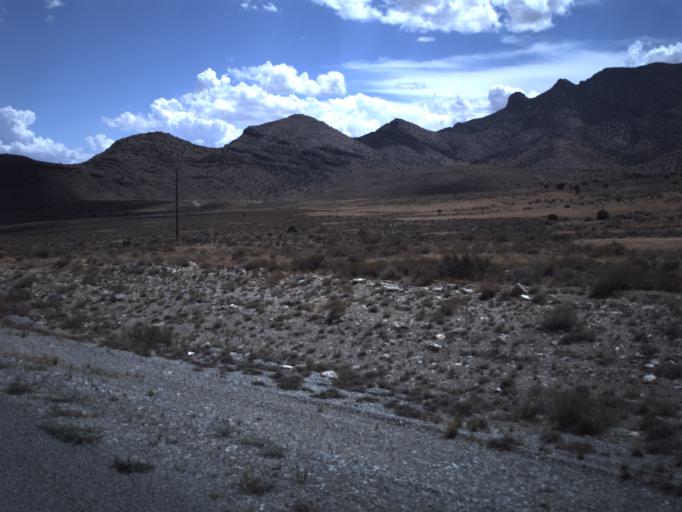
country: US
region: Utah
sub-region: Beaver County
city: Milford
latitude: 39.0873
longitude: -113.5434
